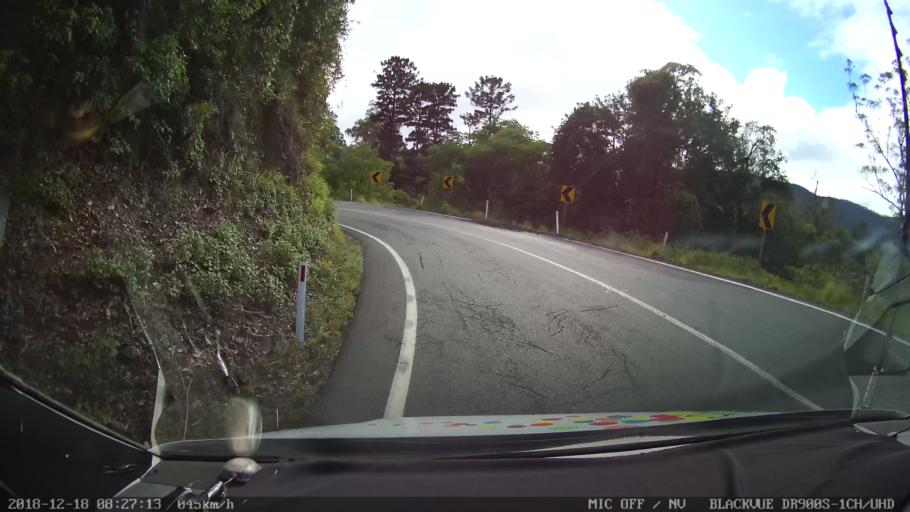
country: AU
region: New South Wales
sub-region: Kyogle
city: Kyogle
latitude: -28.3262
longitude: 152.7483
